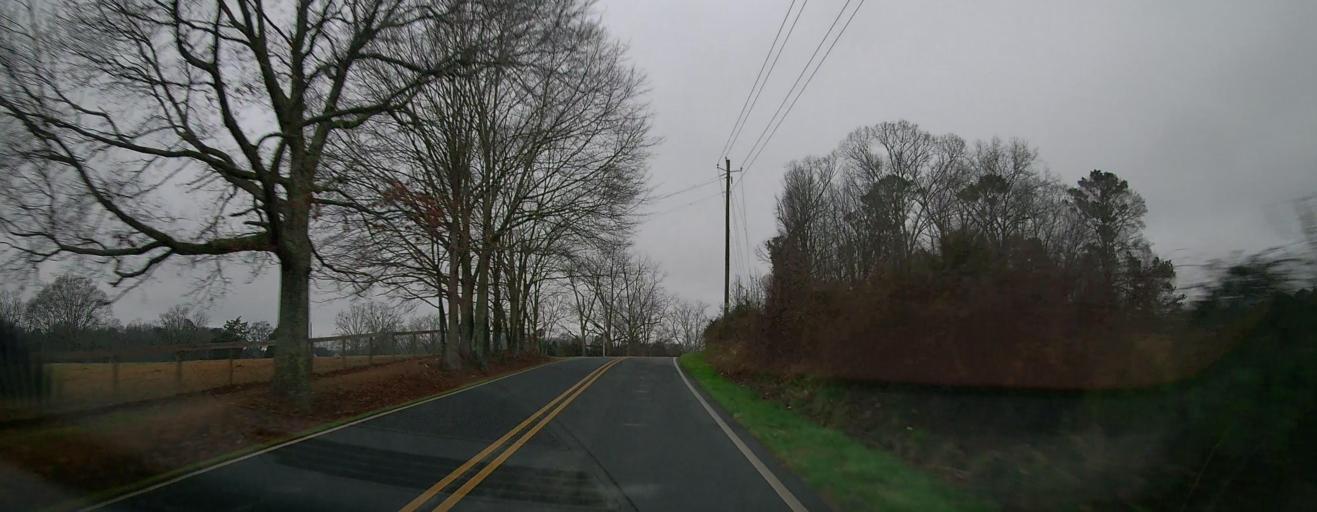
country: US
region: Georgia
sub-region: Pike County
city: Zebulon
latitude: 33.1518
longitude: -84.3519
